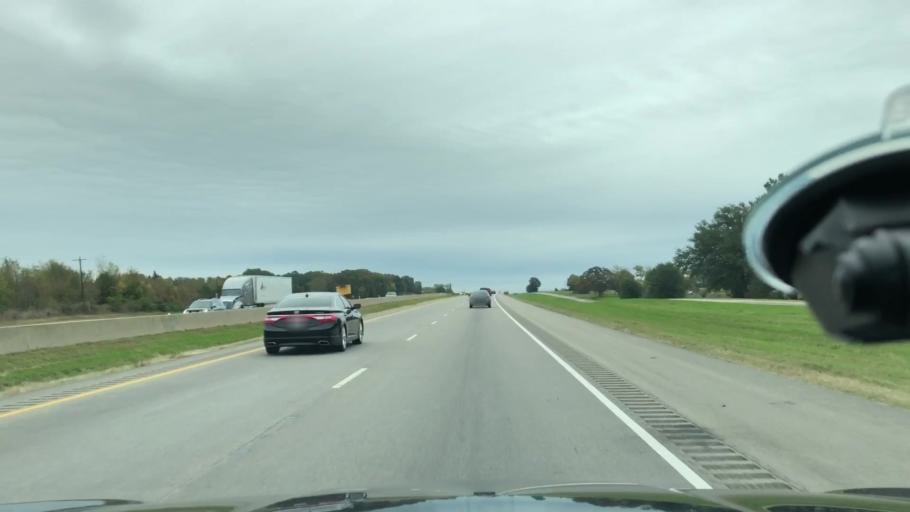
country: US
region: Texas
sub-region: Franklin County
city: Mount Vernon
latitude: 33.1645
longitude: -95.2778
